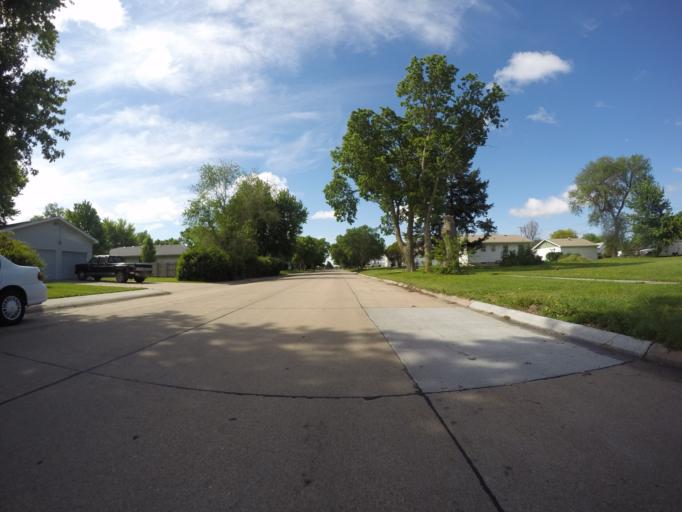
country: US
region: Nebraska
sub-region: Buffalo County
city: Kearney
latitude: 40.6879
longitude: -99.0874
